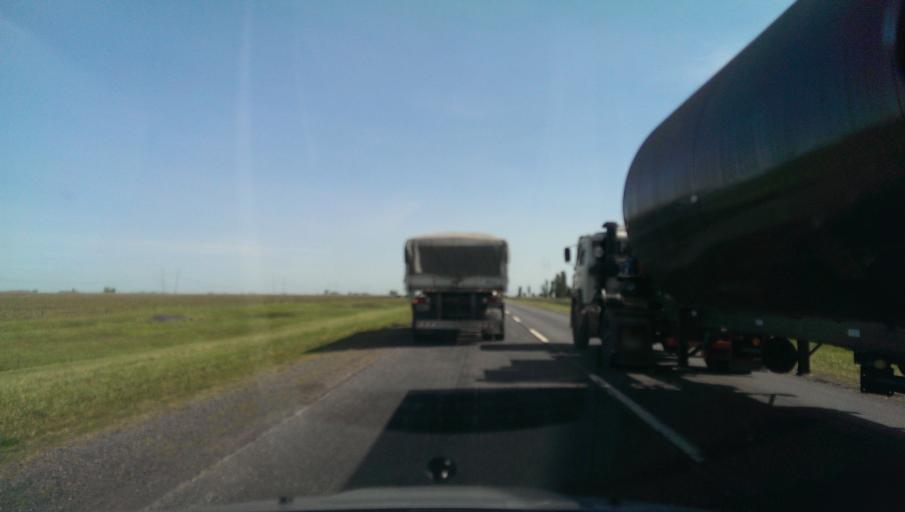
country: AR
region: Buenos Aires
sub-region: Partido de Azul
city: Azul
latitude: -36.6125
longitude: -59.6795
